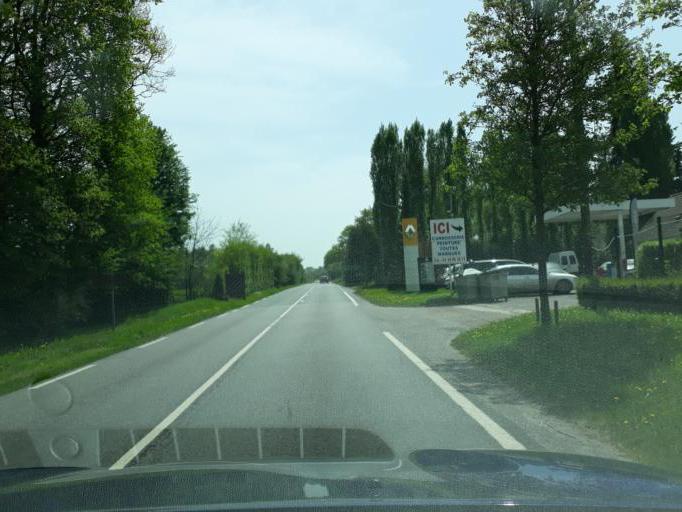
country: FR
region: Ile-de-France
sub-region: Departement des Yvelines
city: Saint-Leger-en-Yvelines
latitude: 48.7125
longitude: 1.7697
